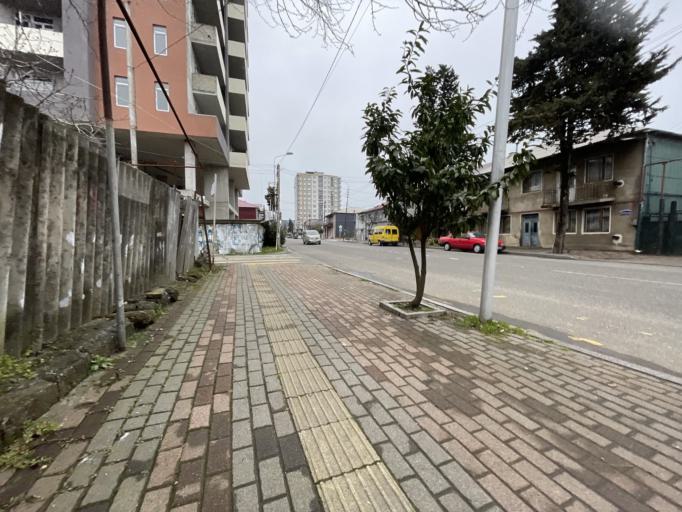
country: GE
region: Ajaria
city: Batumi
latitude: 41.6395
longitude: 41.6417
